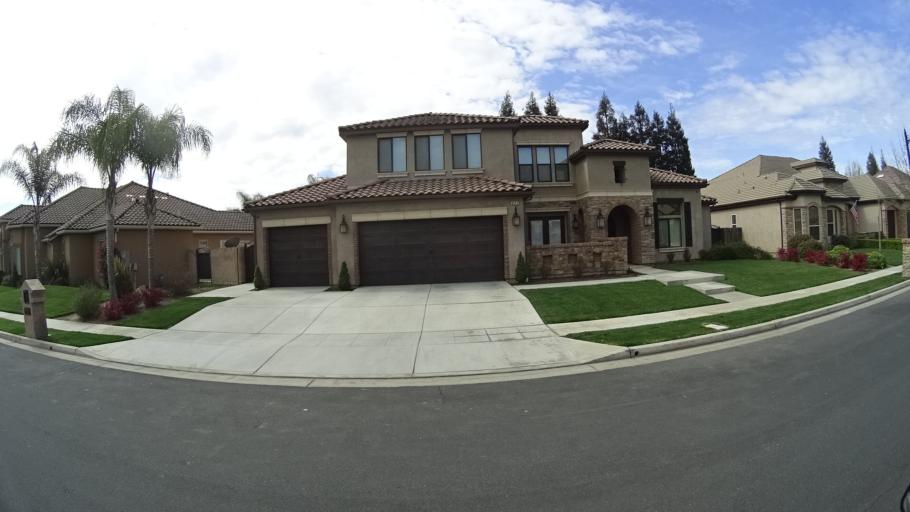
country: US
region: California
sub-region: Madera County
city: Bonadelle Ranchos-Madera Ranchos
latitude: 36.8490
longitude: -119.8833
